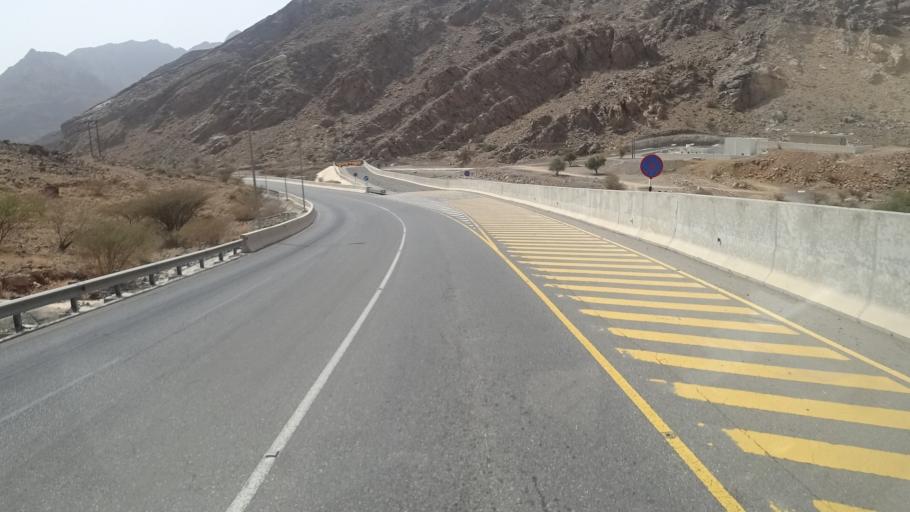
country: OM
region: Muhafazat ad Dakhiliyah
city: Izki
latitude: 22.9626
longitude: 57.6804
